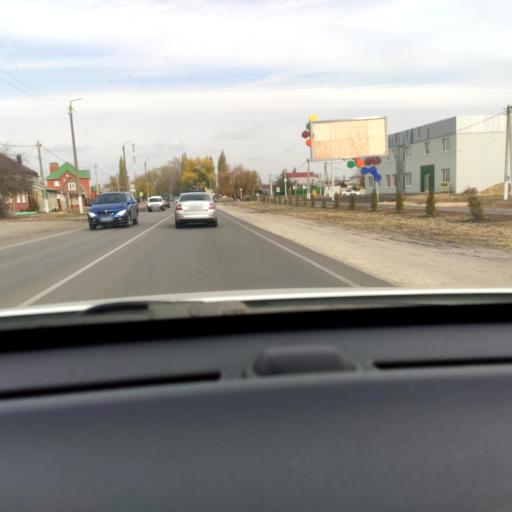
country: RU
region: Voronezj
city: Novaya Usman'
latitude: 51.6322
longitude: 39.4030
